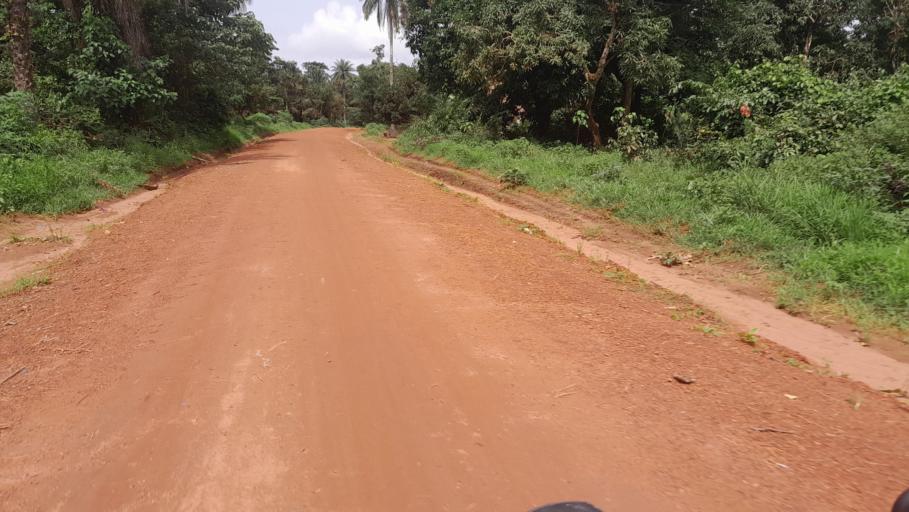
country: GN
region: Boke
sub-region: Boffa
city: Boffa
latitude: 10.0323
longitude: -13.8778
